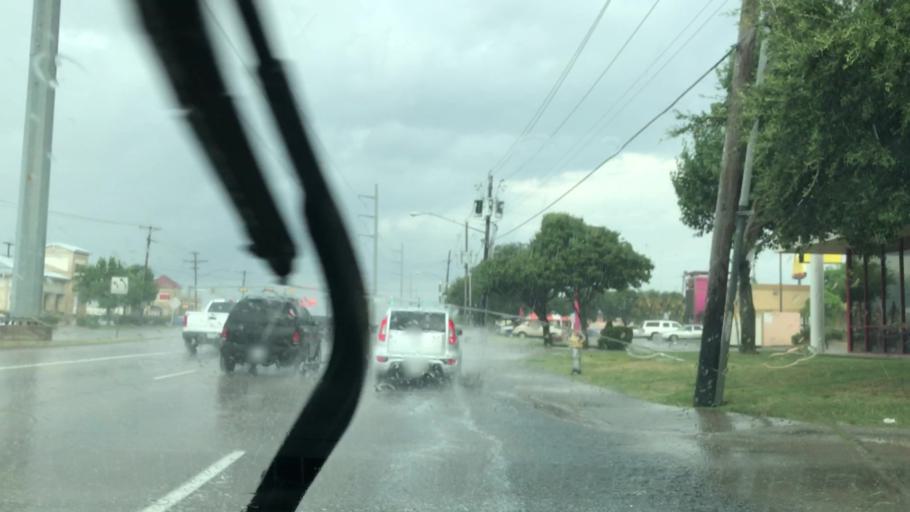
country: US
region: Texas
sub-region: Dallas County
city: Richardson
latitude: 32.9090
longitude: -96.7021
